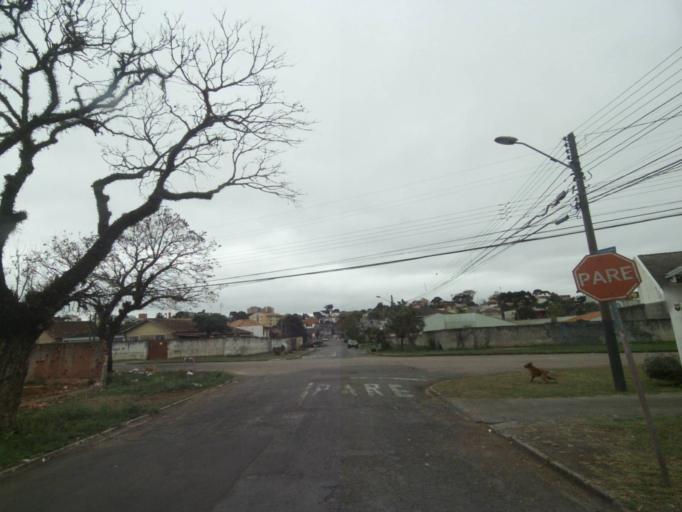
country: BR
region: Parana
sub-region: Curitiba
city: Curitiba
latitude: -25.4634
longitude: -49.2732
